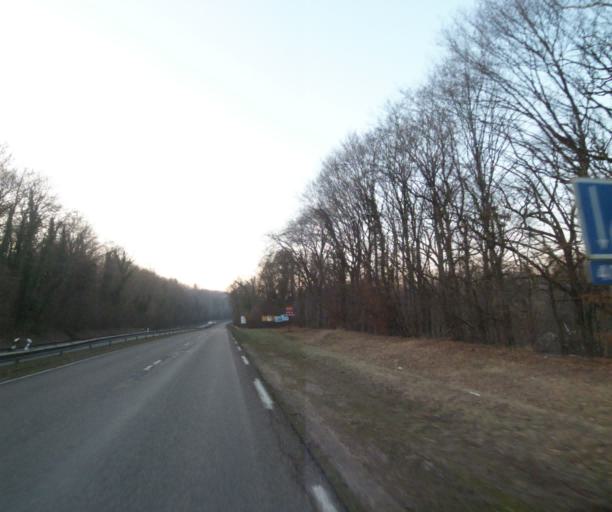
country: FR
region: Lorraine
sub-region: Departement de la Meuse
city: Ancerville
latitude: 48.6106
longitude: 5.0079
